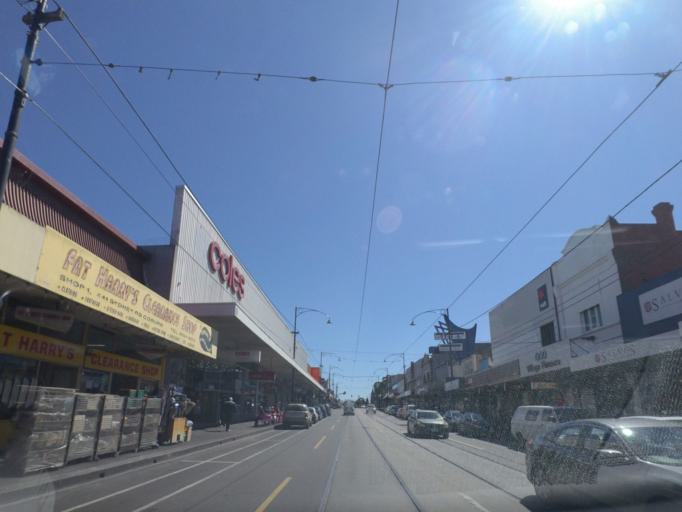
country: AU
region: Victoria
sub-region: Moreland
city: Coburg
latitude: -37.7428
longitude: 144.9663
